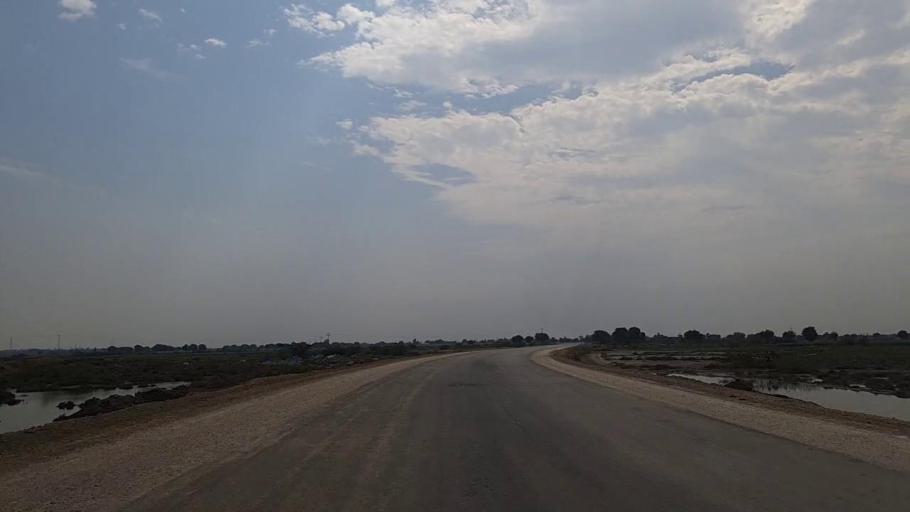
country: PK
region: Sindh
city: Naukot
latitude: 24.9889
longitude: 69.2852
